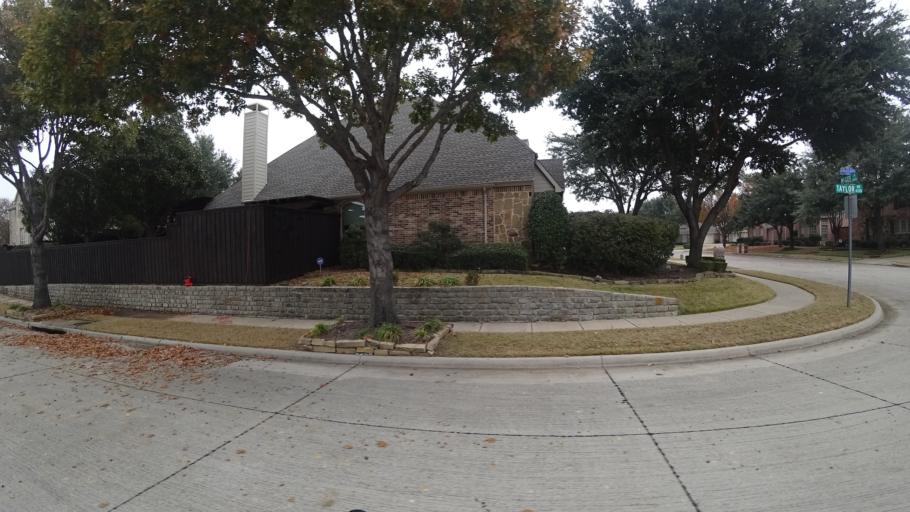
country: US
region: Texas
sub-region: Denton County
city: Lewisville
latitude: 33.0297
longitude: -96.9376
